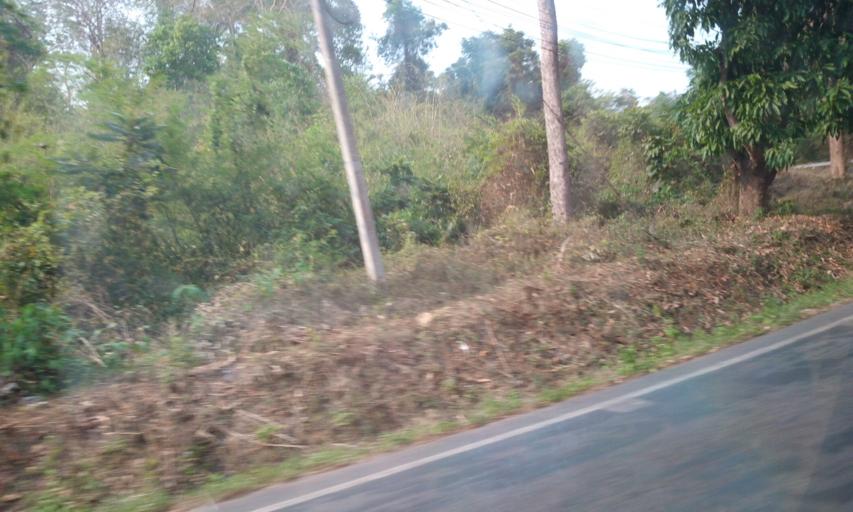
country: TH
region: Chiang Rai
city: Pa Daet
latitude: 19.6150
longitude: 100.0018
